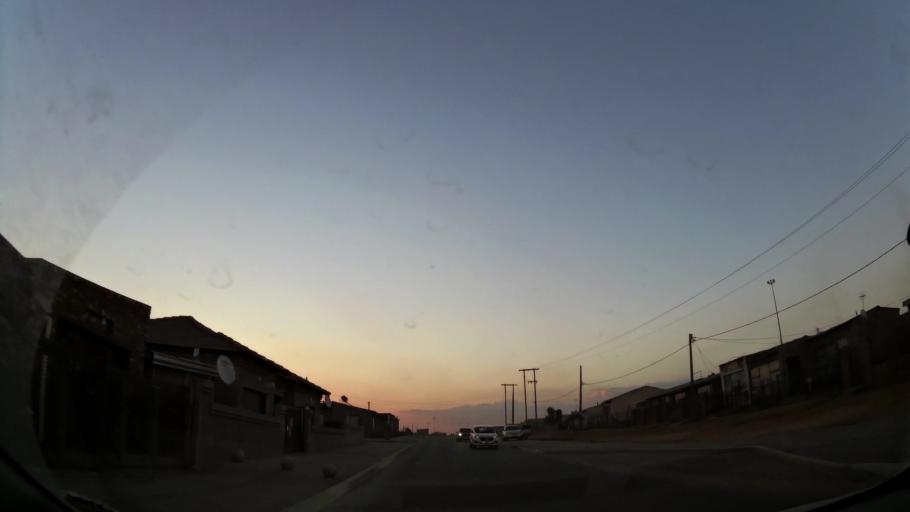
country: ZA
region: Gauteng
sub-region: Ekurhuleni Metropolitan Municipality
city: Nigel
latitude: -26.3716
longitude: 28.4000
